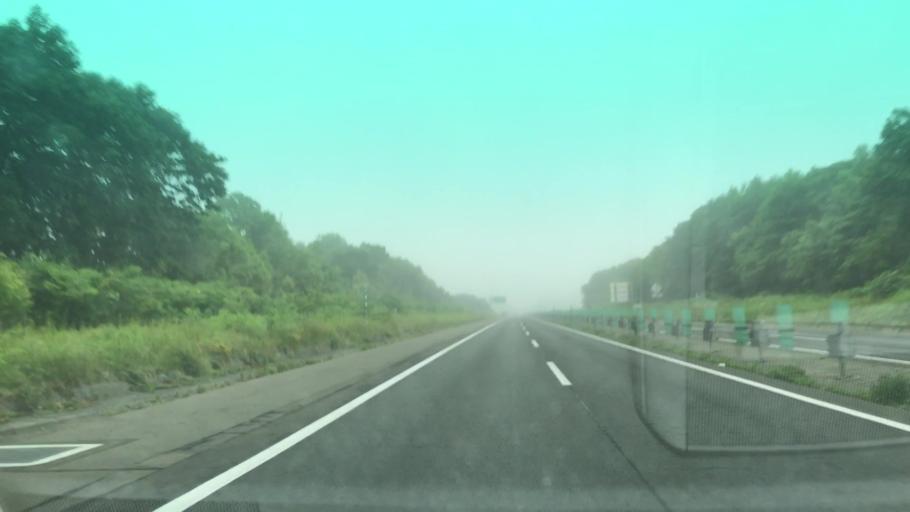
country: JP
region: Hokkaido
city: Chitose
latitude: 42.8228
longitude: 141.6164
